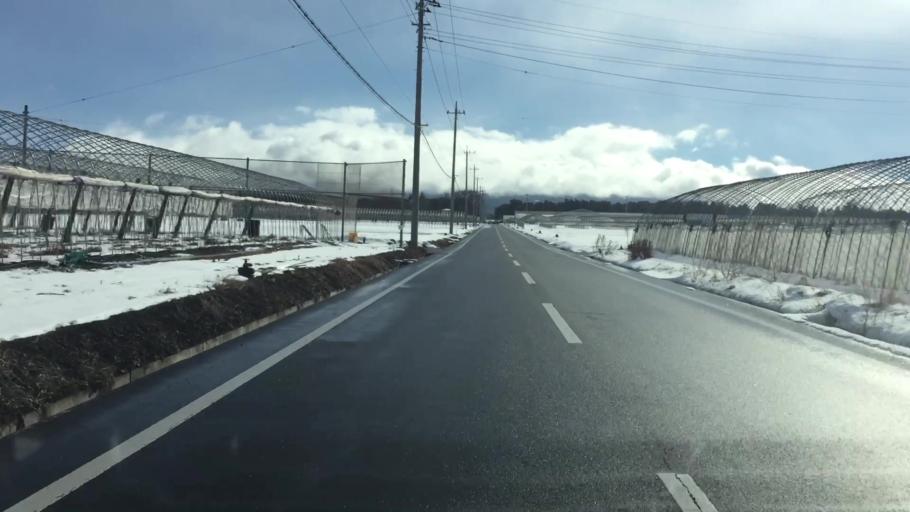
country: JP
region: Gunma
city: Numata
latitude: 36.6310
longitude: 139.0890
